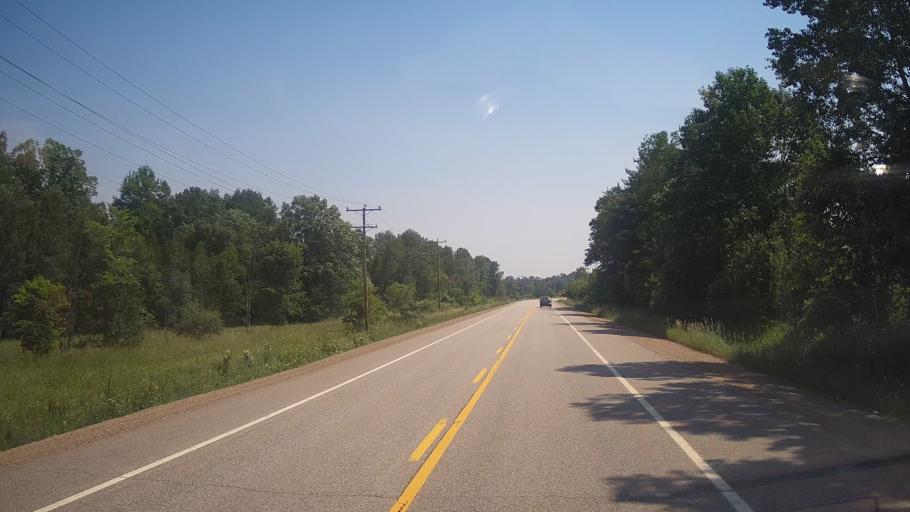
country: CA
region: Ontario
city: Pembroke
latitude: 45.8874
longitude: -76.9480
